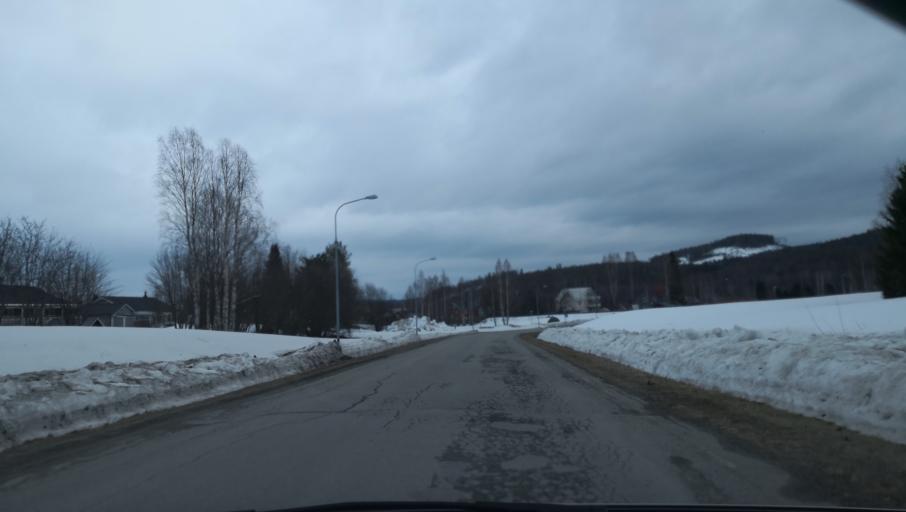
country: SE
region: Vaesterbotten
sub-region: Vannas Kommun
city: Vannasby
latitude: 63.9171
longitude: 19.8103
